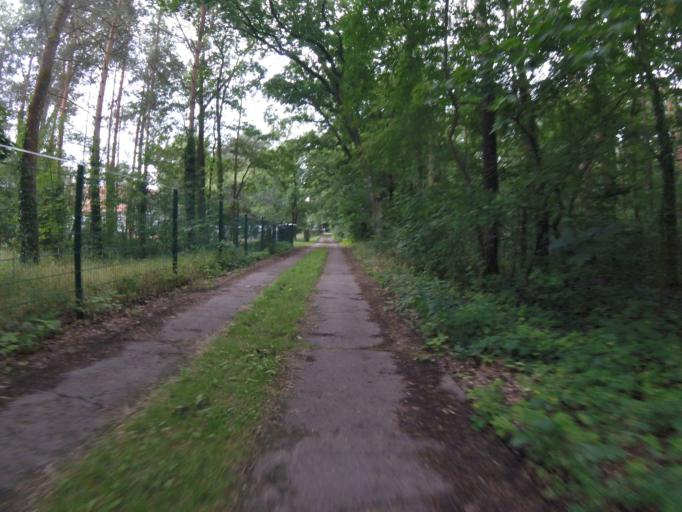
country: DE
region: Brandenburg
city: Konigs Wusterhausen
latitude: 52.2991
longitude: 13.6414
